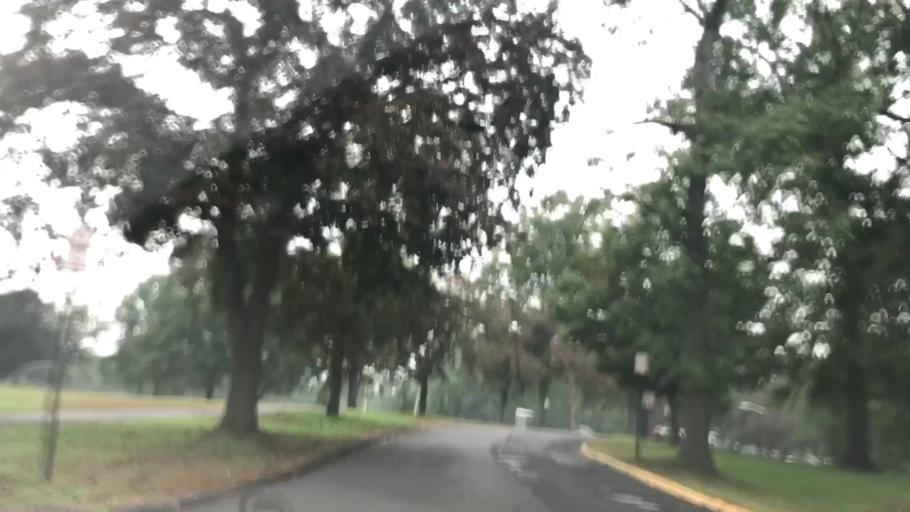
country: US
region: New Jersey
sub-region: Union County
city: Rahway
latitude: 40.6206
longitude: -74.2828
